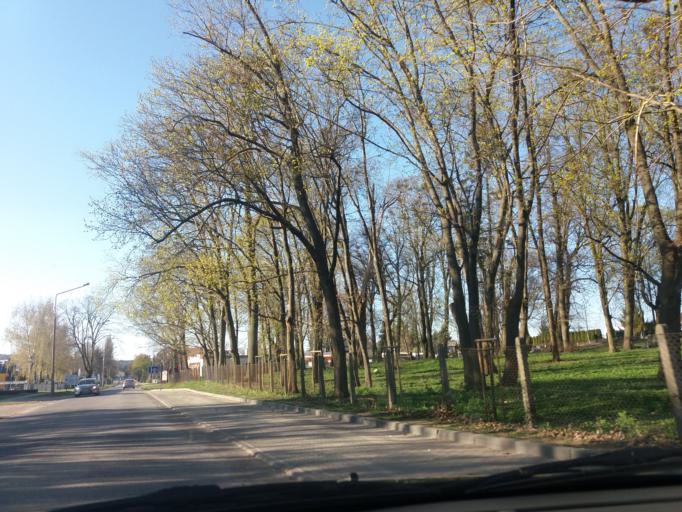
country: PL
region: Warmian-Masurian Voivodeship
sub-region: Powiat nidzicki
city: Nidzica
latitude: 53.3518
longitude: 20.4287
